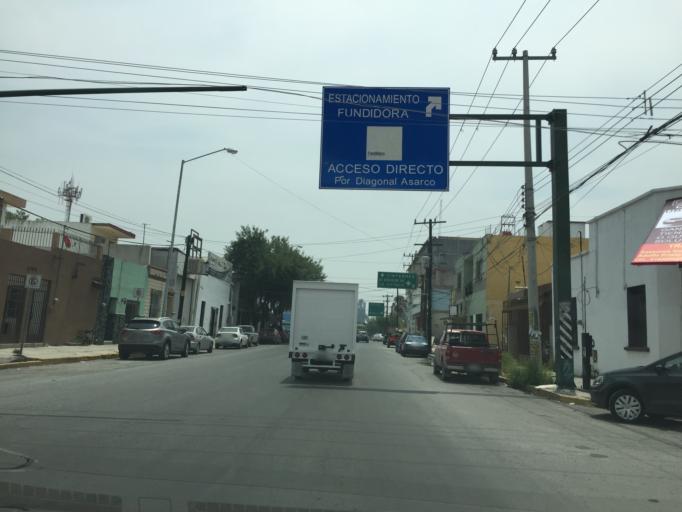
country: MX
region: Nuevo Leon
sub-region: Monterrey
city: Monterrey
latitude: 25.6773
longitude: -100.2928
